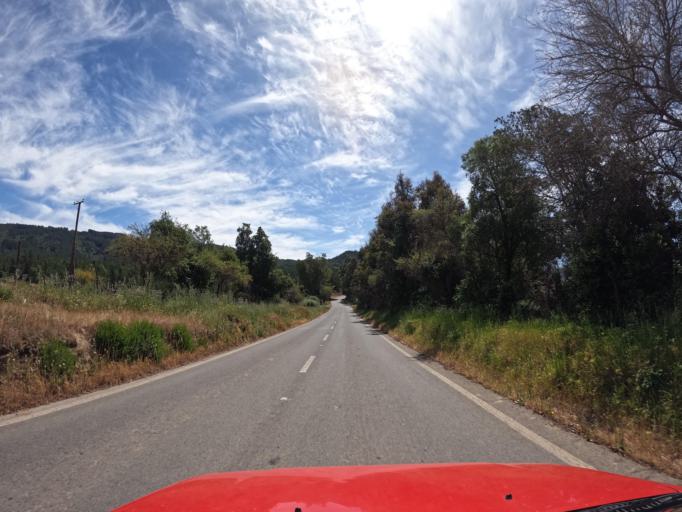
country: CL
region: Maule
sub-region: Provincia de Talca
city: Talca
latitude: -34.9997
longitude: -71.8043
